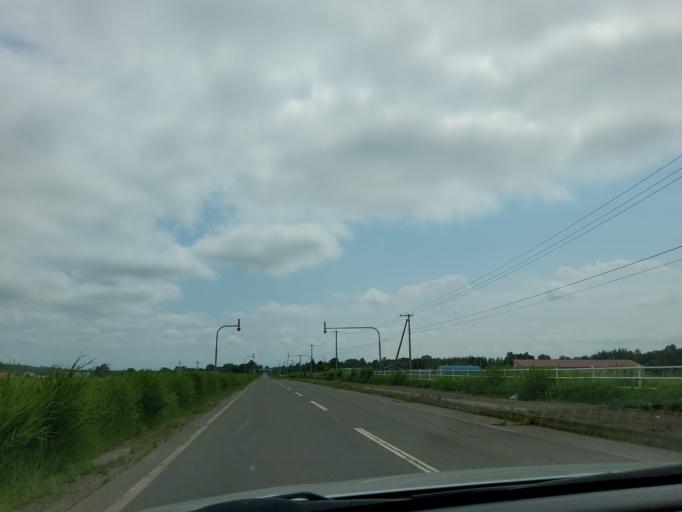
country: JP
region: Hokkaido
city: Obihiro
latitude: 42.8940
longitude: 143.1191
